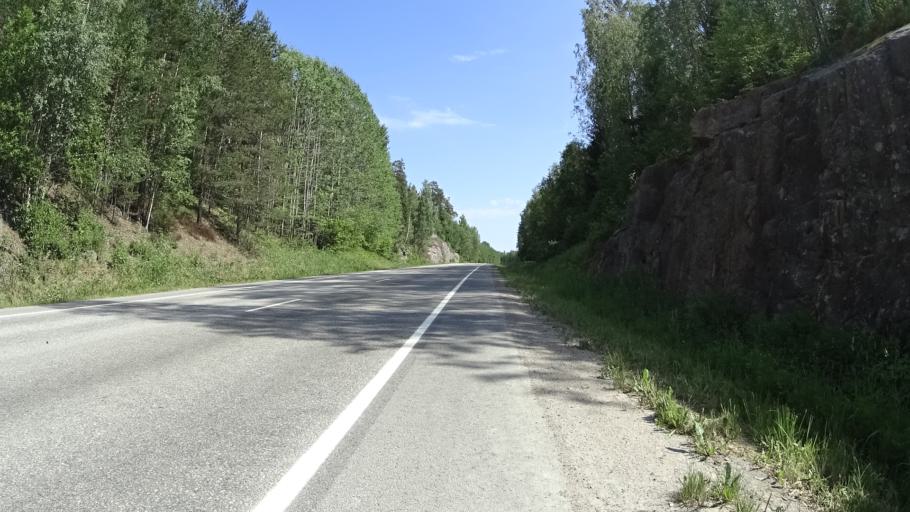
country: FI
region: Uusimaa
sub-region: Raaseporin
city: Karis
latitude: 60.0920
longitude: 23.6389
